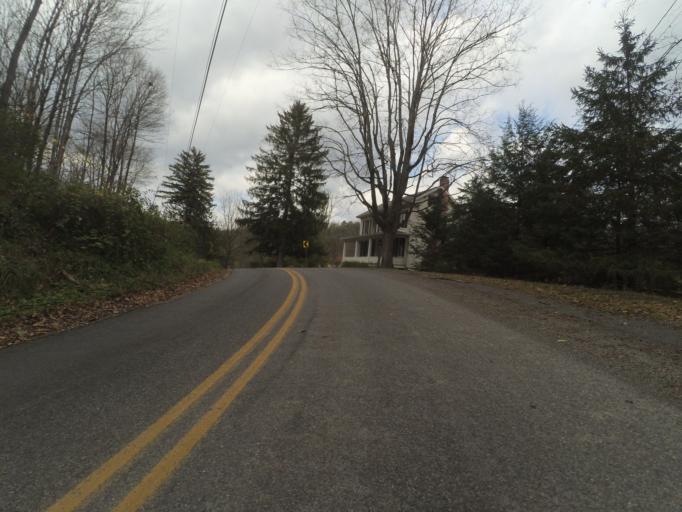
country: US
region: Pennsylvania
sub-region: Centre County
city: Bellefonte
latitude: 40.8936
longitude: -77.7910
